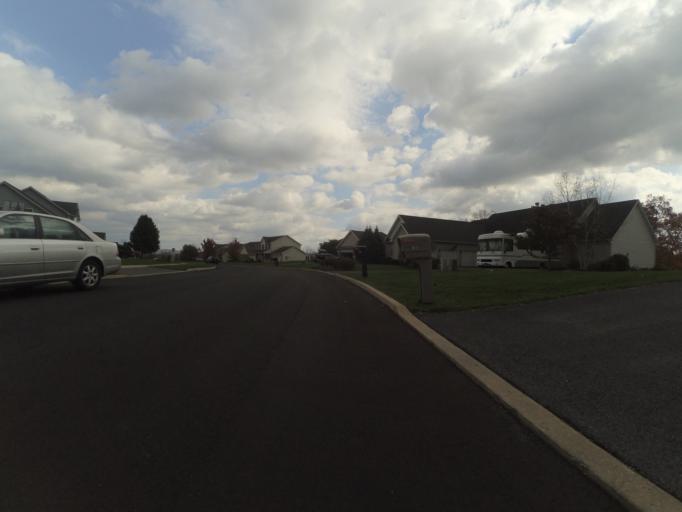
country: US
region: Pennsylvania
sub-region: Centre County
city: Bellefonte
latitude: 40.8933
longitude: -77.8076
